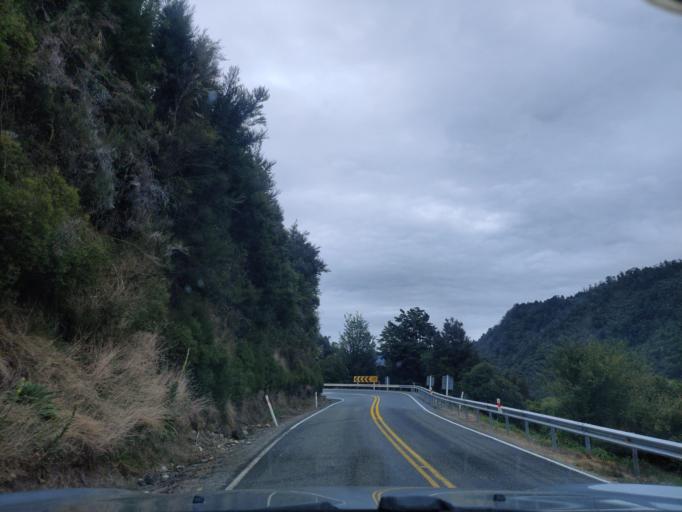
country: NZ
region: Tasman
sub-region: Tasman District
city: Wakefield
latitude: -41.6961
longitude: 172.6169
